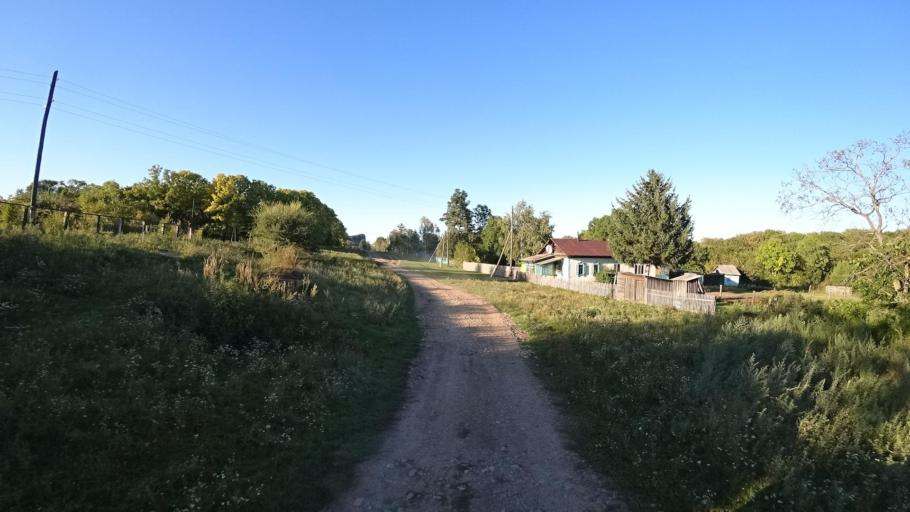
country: RU
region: Primorskiy
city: Kirovskiy
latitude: 44.8265
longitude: 133.5748
